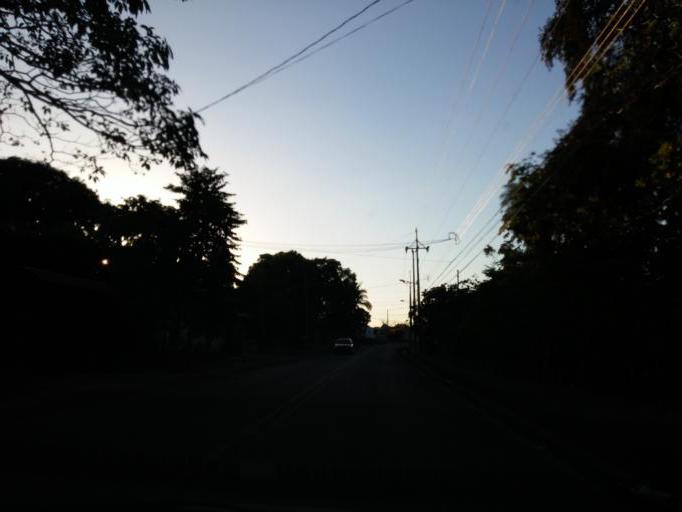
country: CR
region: Alajuela
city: Orotina
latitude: 9.9137
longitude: -84.5265
